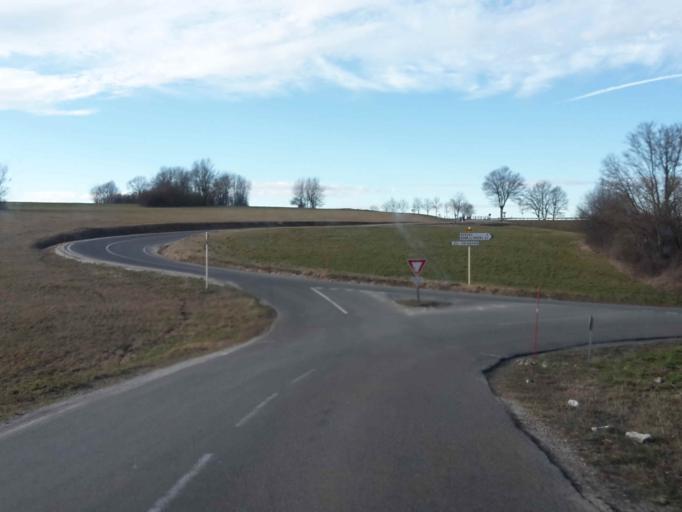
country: FR
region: Franche-Comte
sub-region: Departement du Doubs
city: Valdahon
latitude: 47.1416
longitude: 6.3726
